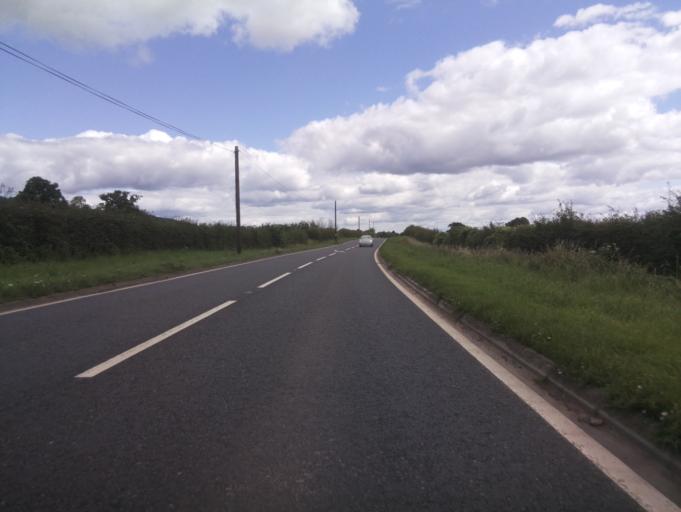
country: GB
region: Wales
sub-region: Monmouthshire
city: Chepstow
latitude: 51.6646
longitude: -2.6333
